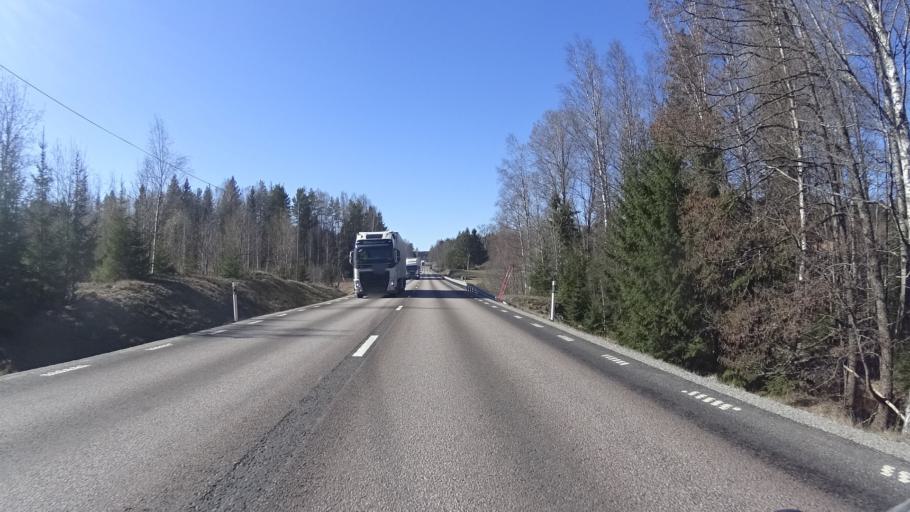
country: SE
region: Vaermland
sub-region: Sunne Kommun
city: Sunne
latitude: 59.6615
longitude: 12.9270
